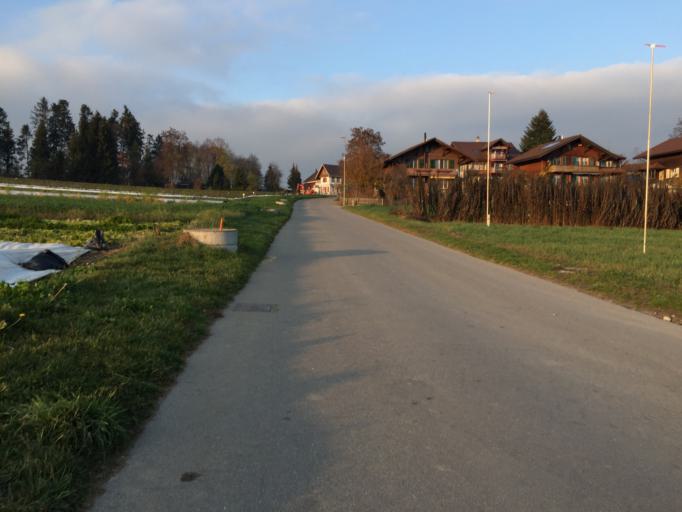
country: CH
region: Bern
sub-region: Bern-Mittelland District
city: Taegertschi
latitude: 46.8810
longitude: 7.5798
